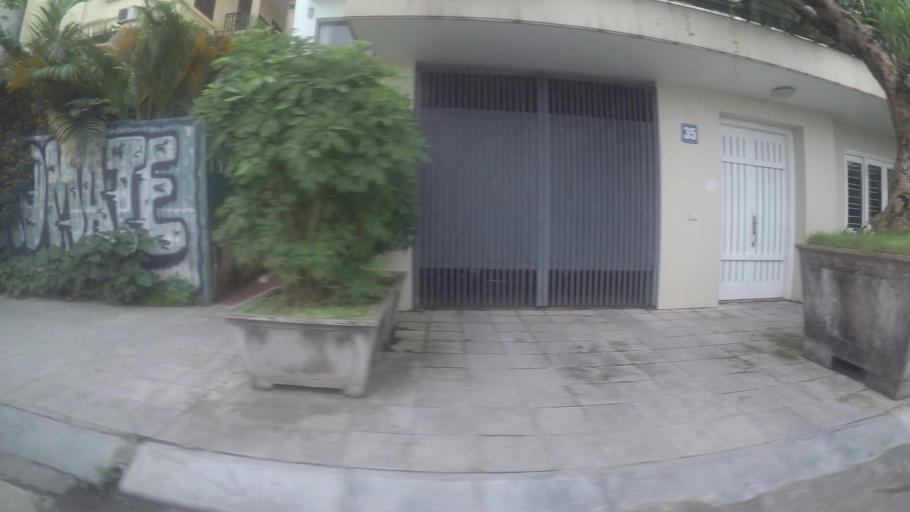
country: VN
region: Ha Noi
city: Tay Ho
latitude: 21.0611
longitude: 105.8195
